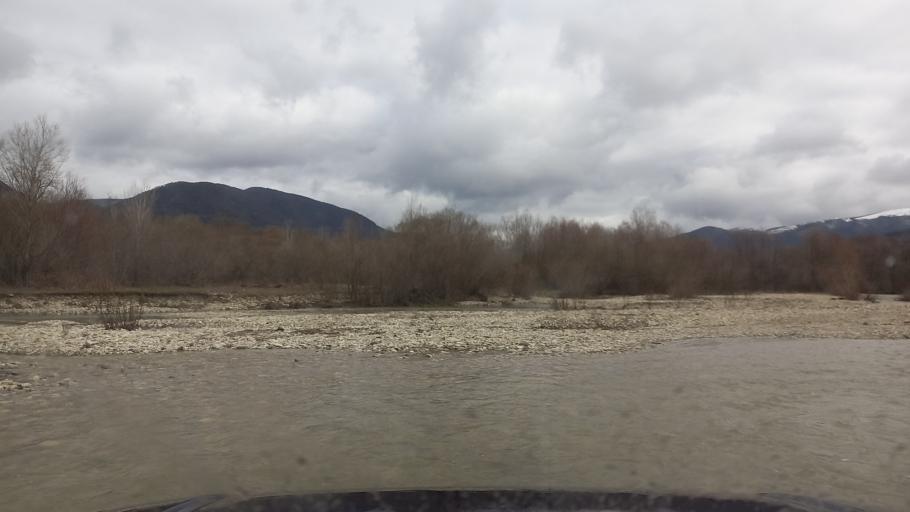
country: RU
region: Krasnodarskiy
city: Pshada
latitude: 44.4865
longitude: 38.4099
